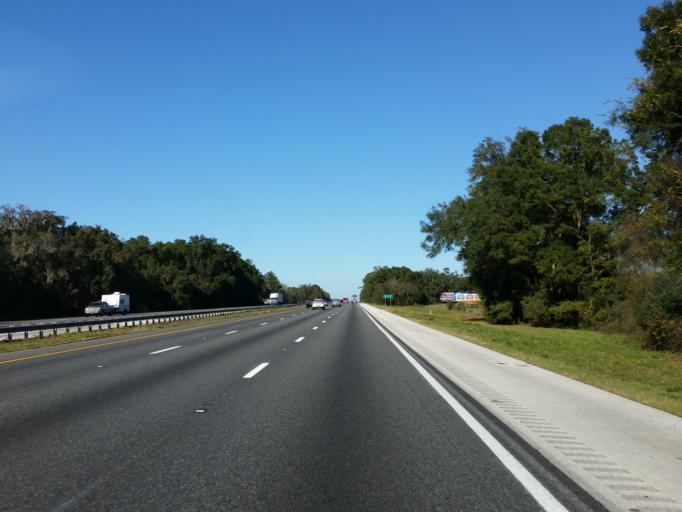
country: US
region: Florida
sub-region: Marion County
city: Ocala
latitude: 29.1079
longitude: -82.1848
